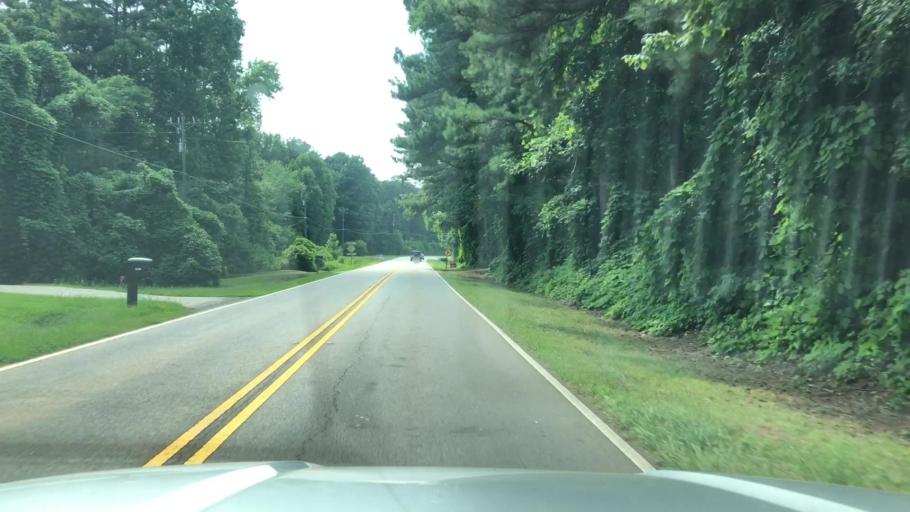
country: US
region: Georgia
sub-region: Paulding County
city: Hiram
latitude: 33.9390
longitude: -84.7599
